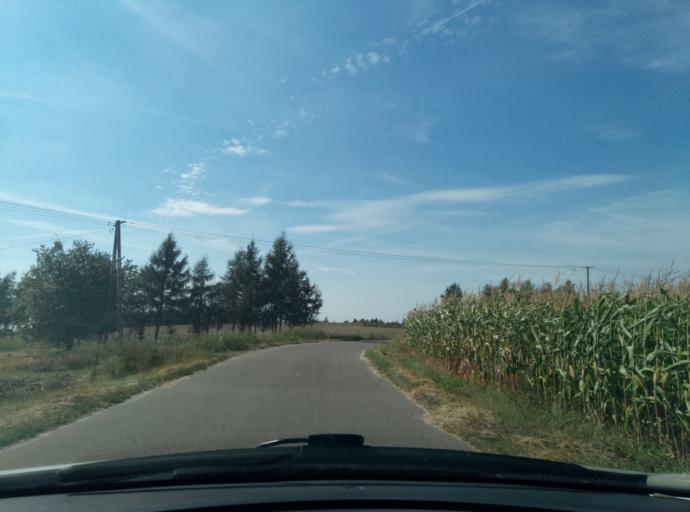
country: PL
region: Kujawsko-Pomorskie
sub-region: Powiat brodnicki
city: Jablonowo Pomorskie
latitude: 53.4114
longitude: 19.2604
